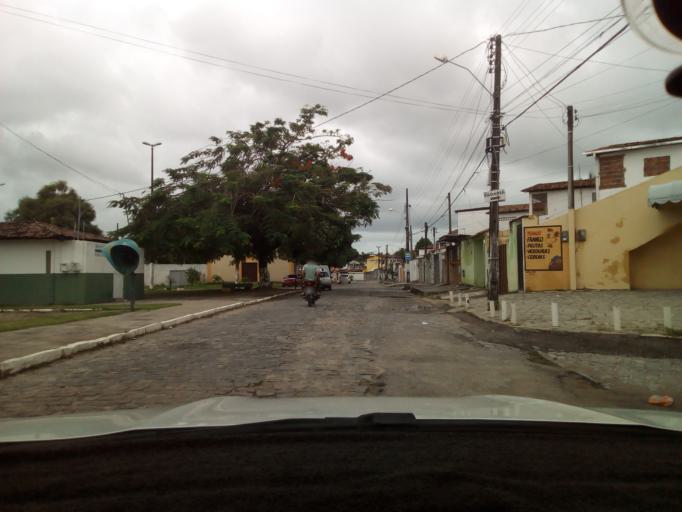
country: BR
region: Paraiba
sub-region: Joao Pessoa
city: Joao Pessoa
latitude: -7.1711
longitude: -34.8885
